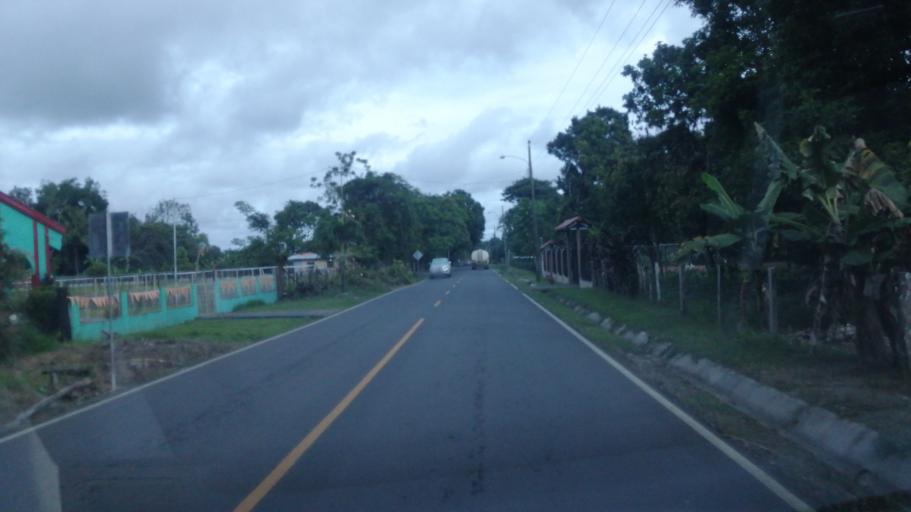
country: PA
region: Chiriqui
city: Alanje
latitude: 8.4172
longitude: -82.5196
